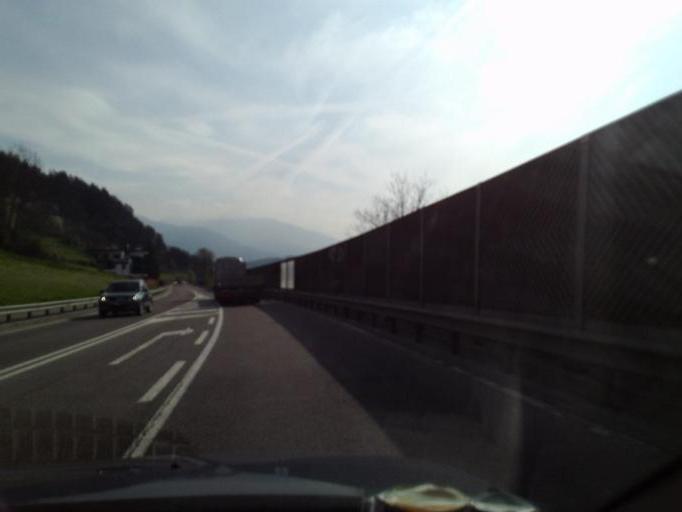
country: IT
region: Trentino-Alto Adige
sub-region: Bolzano
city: San Lorenzo di Sebato
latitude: 46.7843
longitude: 11.8986
